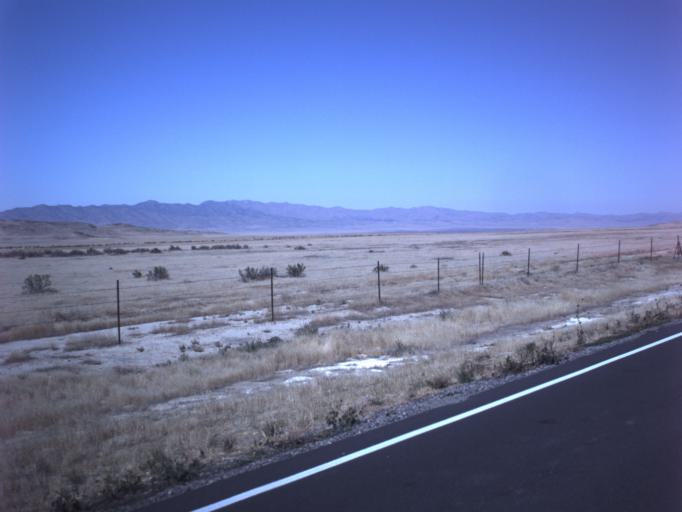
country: US
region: Utah
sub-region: Tooele County
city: Grantsville
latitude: 40.3733
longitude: -112.7465
